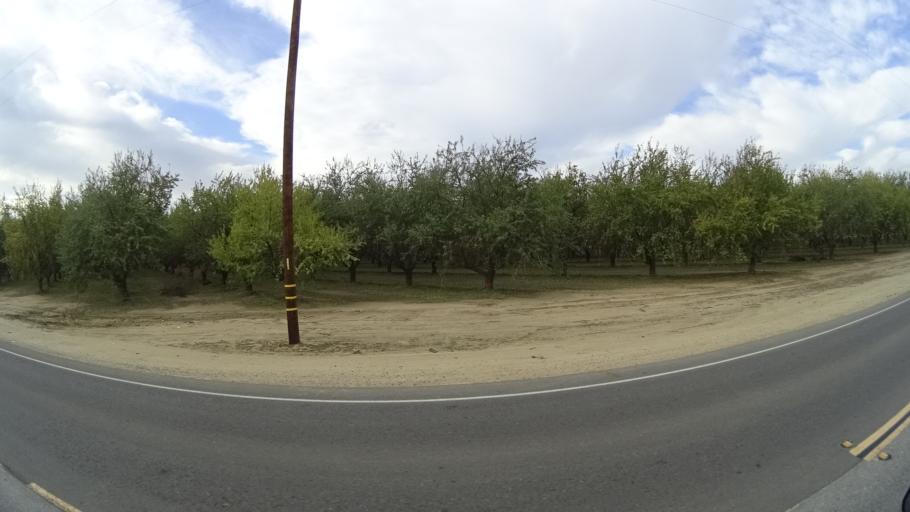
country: US
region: California
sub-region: Kern County
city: Rosedale
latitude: 35.4405
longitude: -119.1977
